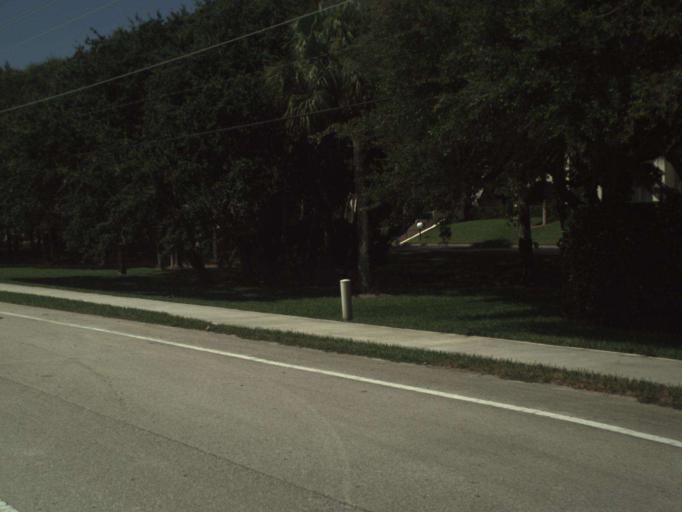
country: US
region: Florida
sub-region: Indian River County
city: Indian River Shores
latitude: 27.6876
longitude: -80.3691
